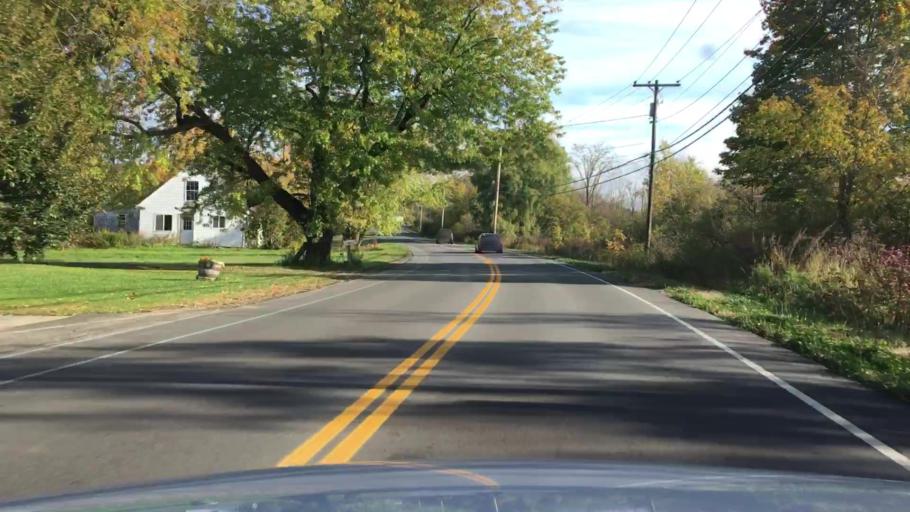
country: US
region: Maine
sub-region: Knox County
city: Thomaston
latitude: 44.0881
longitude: -69.1648
